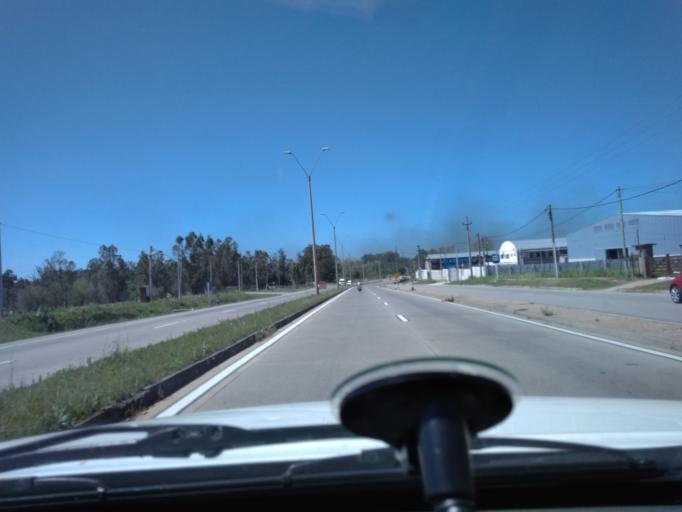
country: UY
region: Canelones
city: Toledo
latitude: -34.7916
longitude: -56.1130
